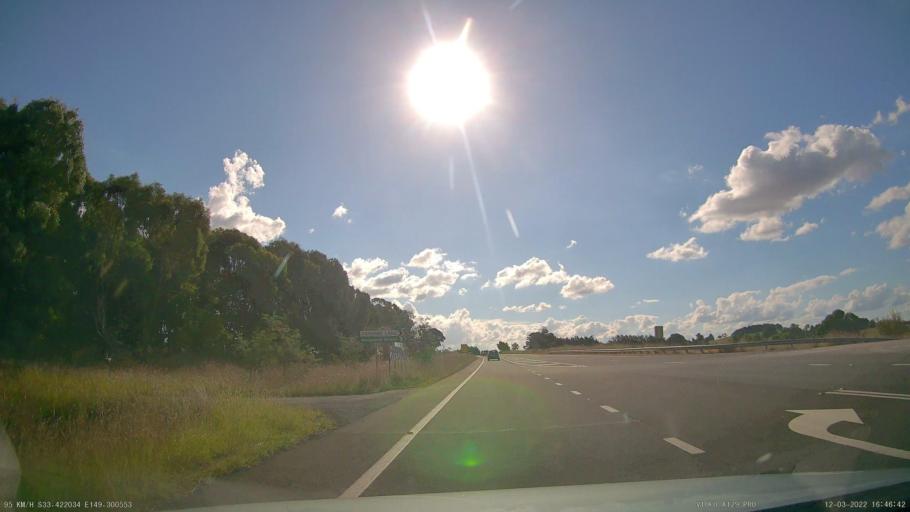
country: AU
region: New South Wales
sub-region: Blayney
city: Millthorpe
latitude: -33.4222
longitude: 149.3001
